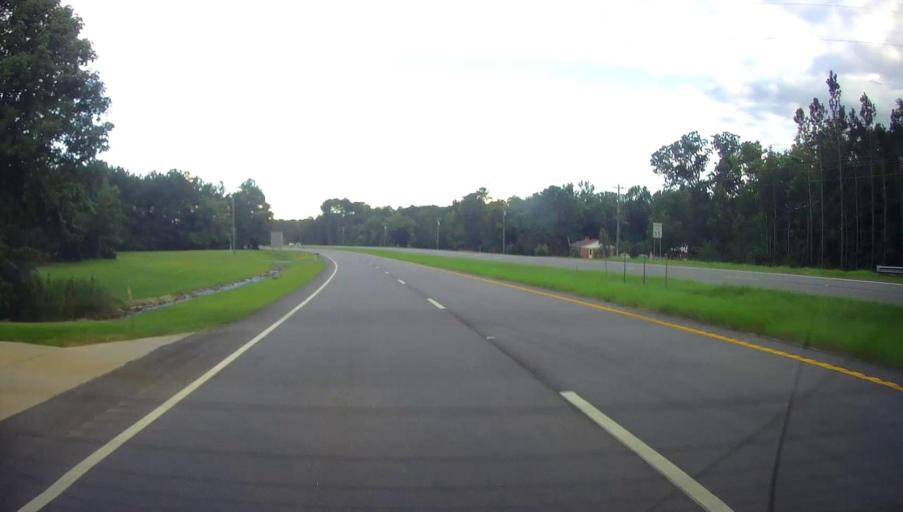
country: US
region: Georgia
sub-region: Houston County
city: Perry
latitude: 32.3720
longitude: -83.6170
